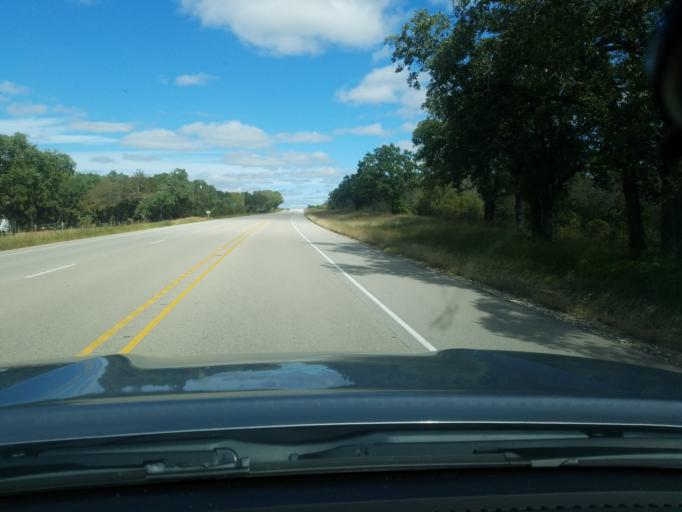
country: US
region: Texas
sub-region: Hamilton County
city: Hamilton
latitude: 31.6177
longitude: -98.1582
